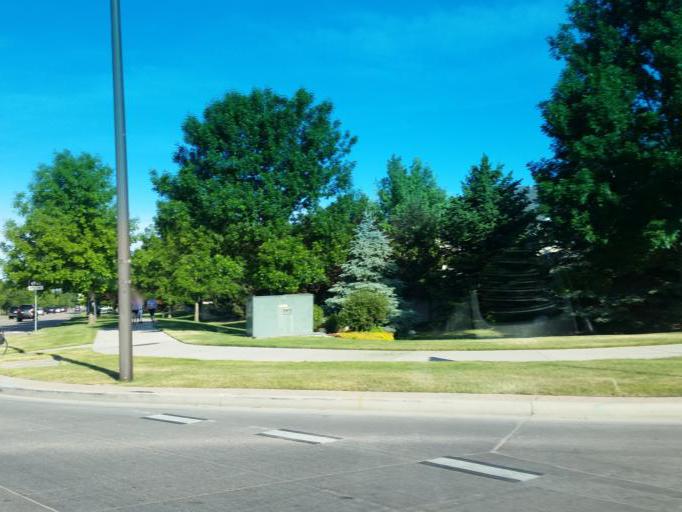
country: US
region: Colorado
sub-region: Larimer County
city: Fort Collins
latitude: 40.5380
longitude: -105.0202
